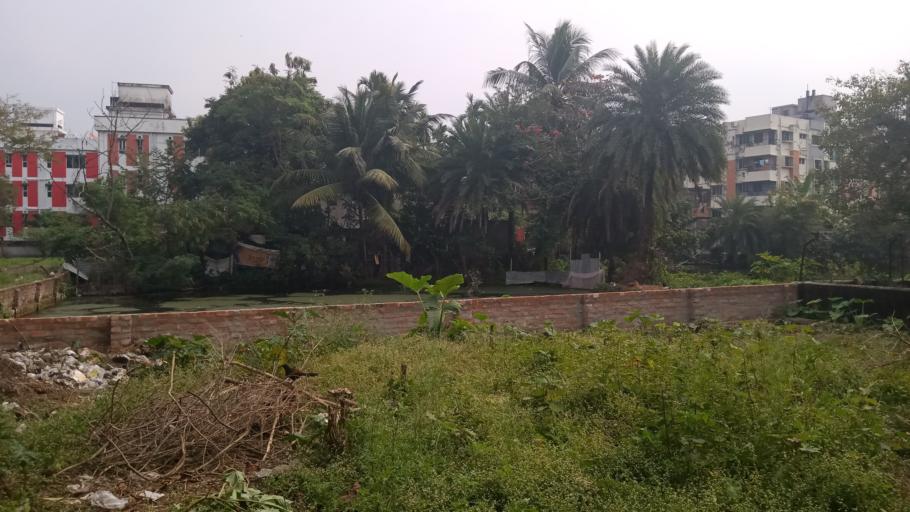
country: IN
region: West Bengal
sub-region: Kolkata
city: Kolkata
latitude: 22.4667
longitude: 88.3832
